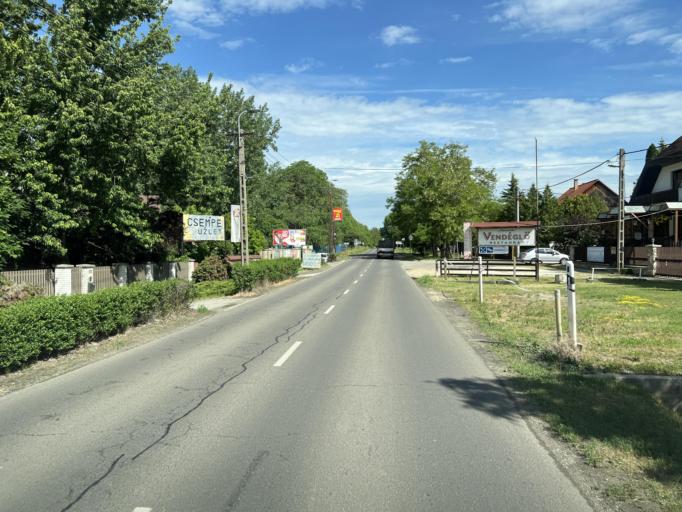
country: HU
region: Pest
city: Isaszeg
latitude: 47.5489
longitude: 19.3869
